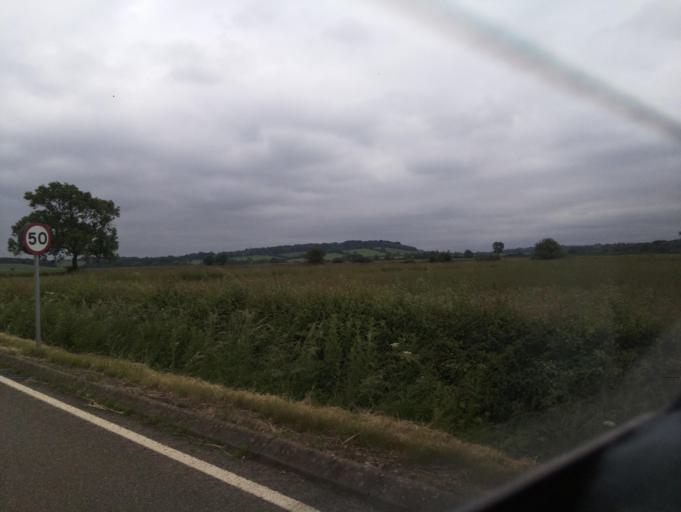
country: GB
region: England
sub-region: Leicestershire
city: Melton Mowbray
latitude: 52.7315
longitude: -0.8476
